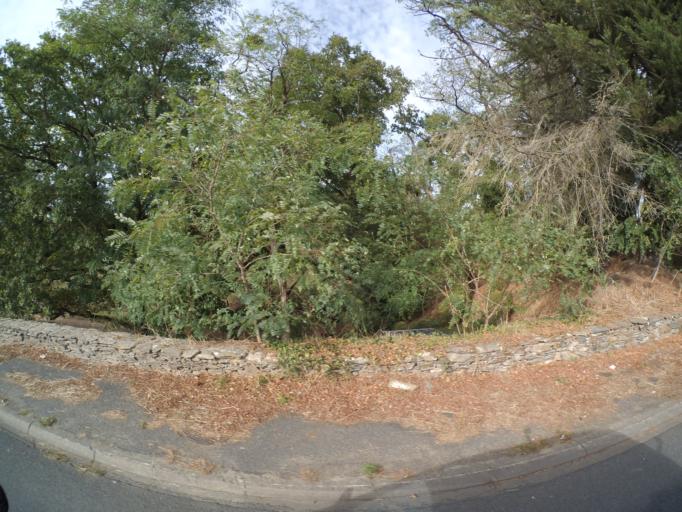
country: FR
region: Pays de la Loire
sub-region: Departement de Maine-et-Loire
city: Villedieu-la-Blouere
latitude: 47.1593
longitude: -1.0527
